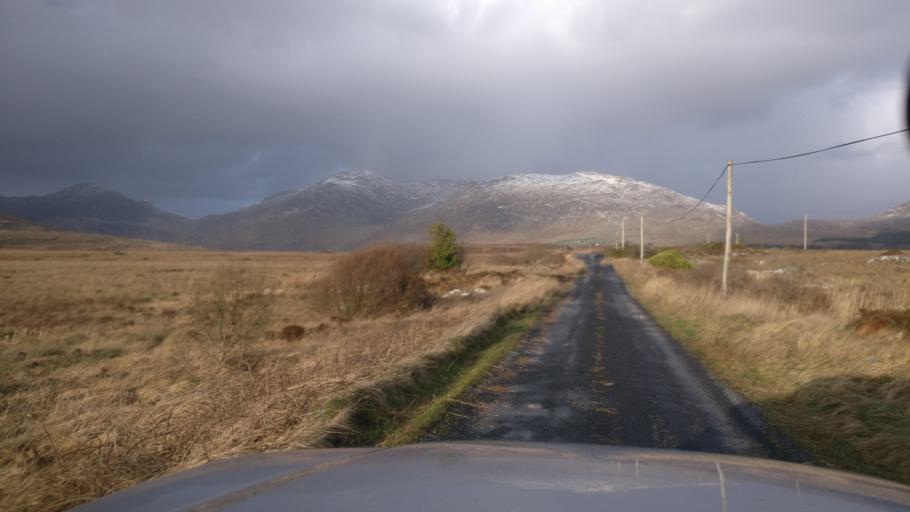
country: IE
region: Connaught
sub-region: County Galway
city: Clifden
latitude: 53.4662
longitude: -9.6974
